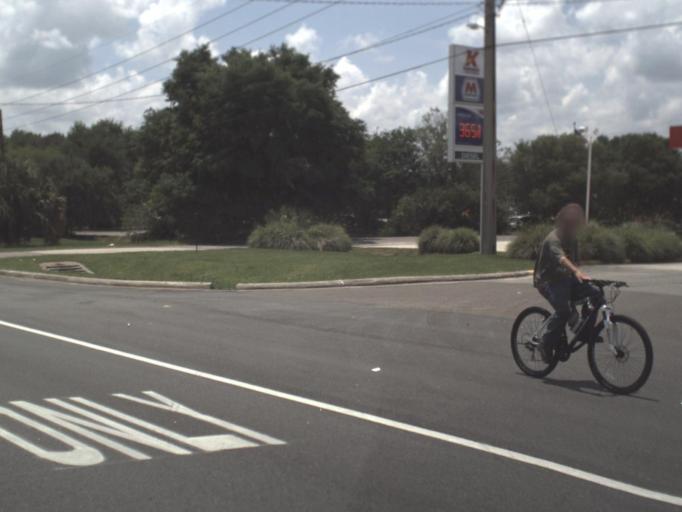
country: US
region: Florida
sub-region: Clay County
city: Bellair-Meadowbrook Terrace
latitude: 30.1935
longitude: -81.7396
